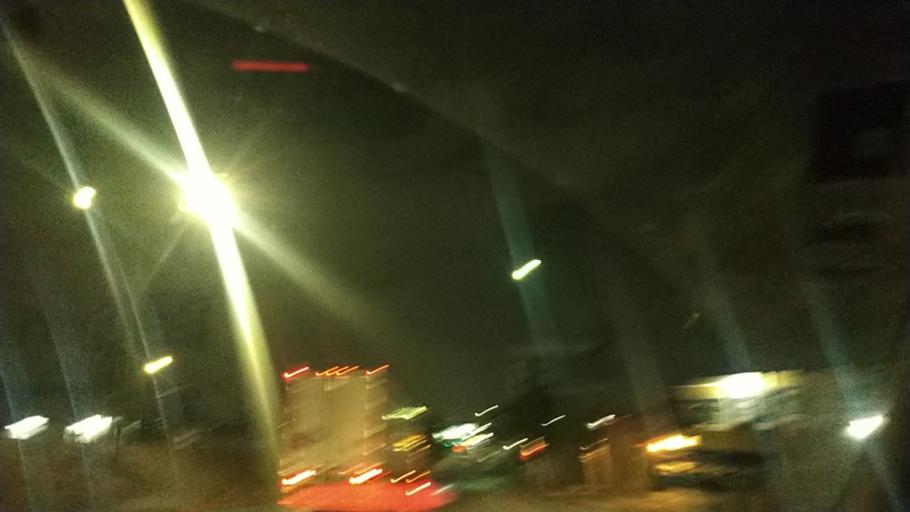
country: MX
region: Mexico
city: Ecatepec
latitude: 19.6196
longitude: -99.0685
